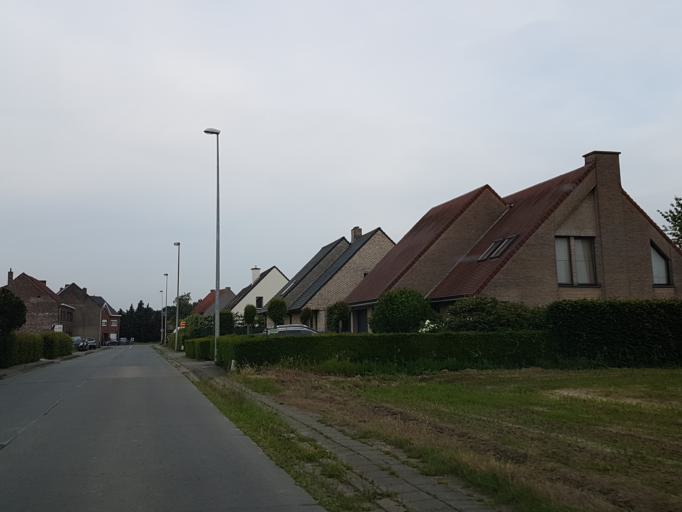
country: BE
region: Flanders
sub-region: Provincie Oost-Vlaanderen
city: Aalst
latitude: 50.9738
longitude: 4.0700
